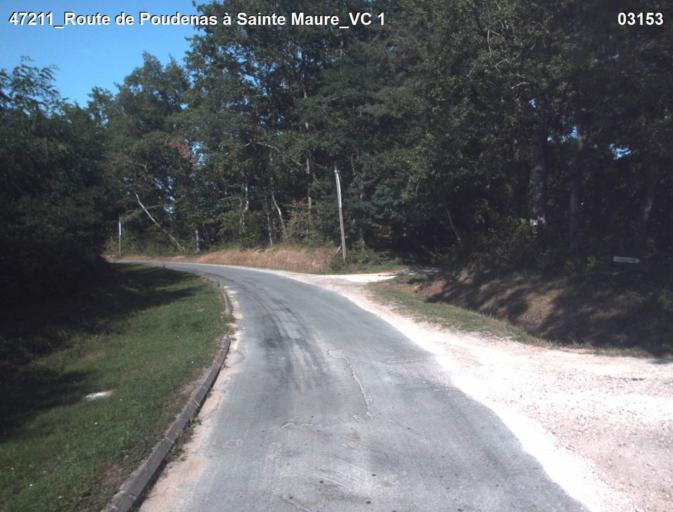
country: FR
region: Aquitaine
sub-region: Departement du Lot-et-Garonne
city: Mezin
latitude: 44.0228
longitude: 0.2002
